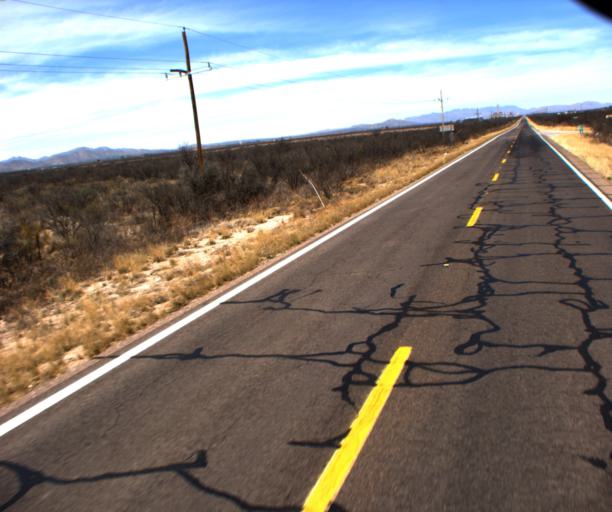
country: US
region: Arizona
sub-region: Cochise County
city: Willcox
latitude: 32.0132
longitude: -109.8675
